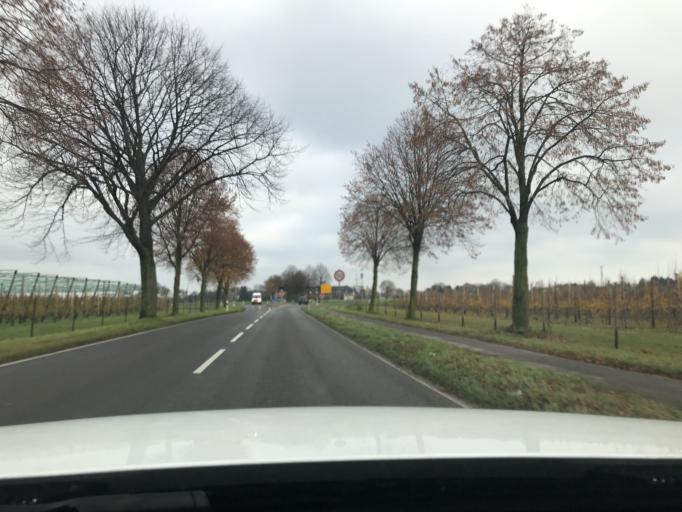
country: DE
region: North Rhine-Westphalia
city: Tonisvorst
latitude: 51.3368
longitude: 6.4952
